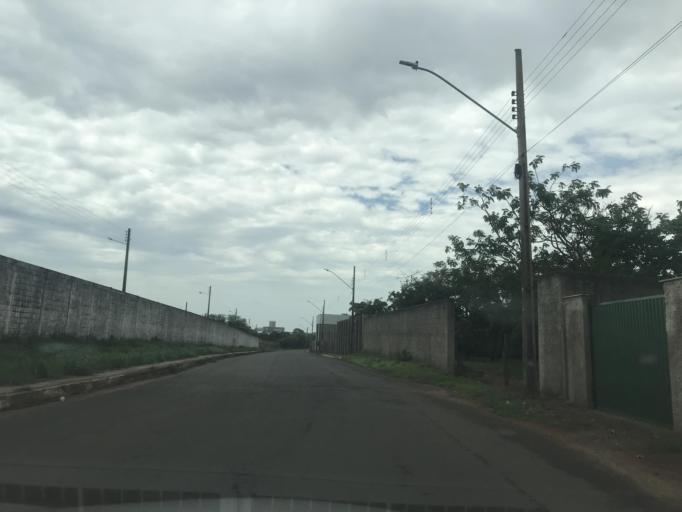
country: BR
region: Goias
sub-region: Luziania
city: Luziania
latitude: -16.2590
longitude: -47.9755
